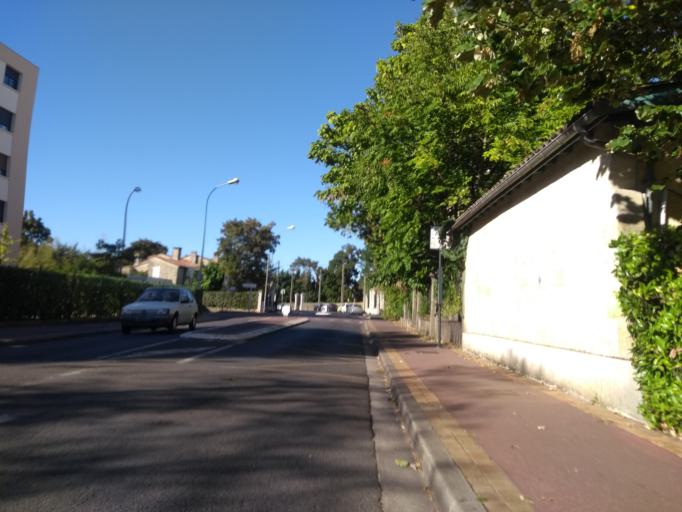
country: FR
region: Aquitaine
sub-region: Departement de la Gironde
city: Talence
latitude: 44.8119
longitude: -0.5861
